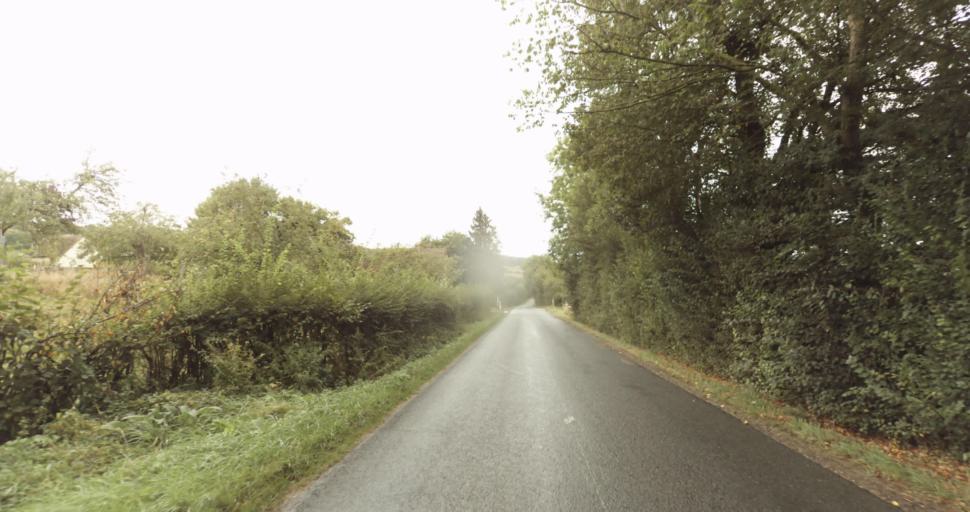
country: FR
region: Lower Normandy
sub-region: Departement de l'Orne
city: Vimoutiers
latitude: 48.8874
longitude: 0.2134
